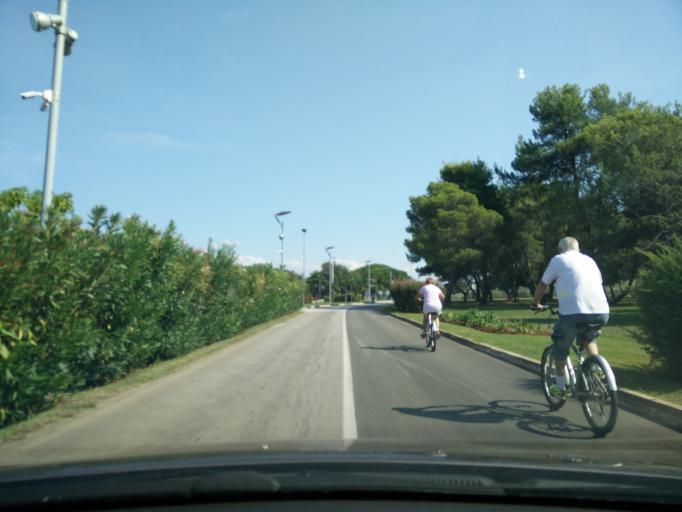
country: HR
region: Istarska
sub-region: Grad Porec
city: Porec
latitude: 45.2018
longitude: 13.5956
